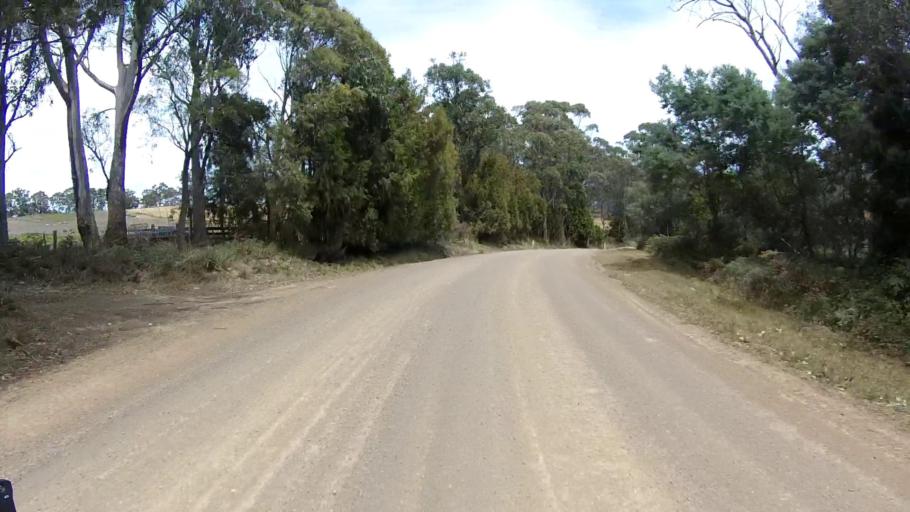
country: AU
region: Tasmania
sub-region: Sorell
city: Sorell
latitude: -42.7923
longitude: 147.6959
